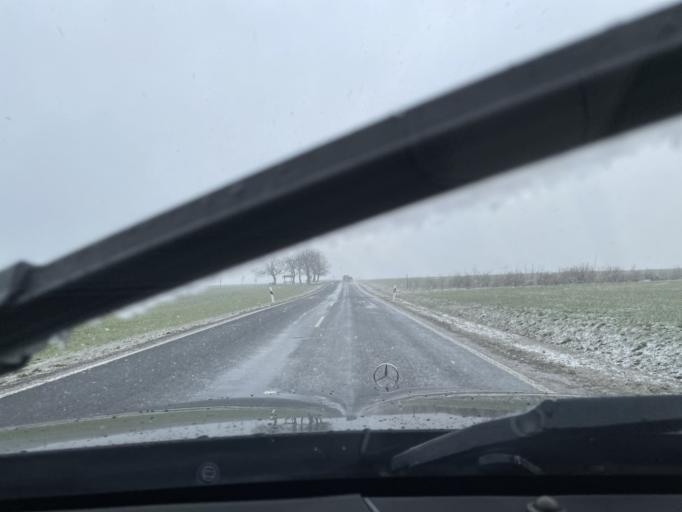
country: DE
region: Thuringia
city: Kullstedt
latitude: 51.2620
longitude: 10.2761
